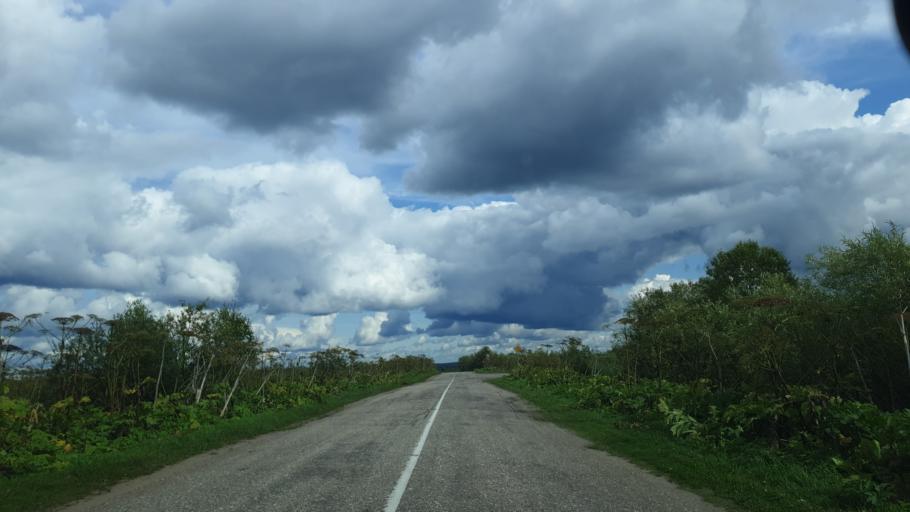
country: RU
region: Komi Republic
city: Aykino
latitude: 61.9565
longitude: 50.1826
